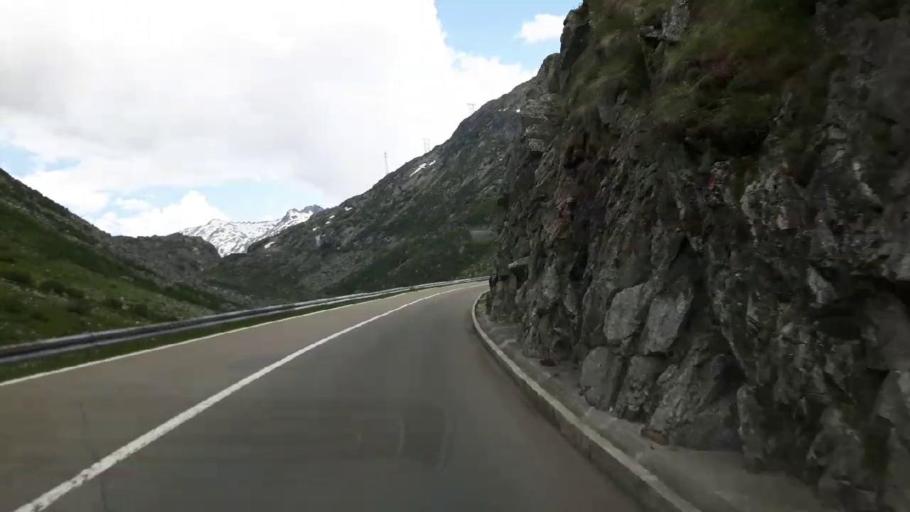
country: CH
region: Uri
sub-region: Uri
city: Andermatt
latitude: 46.5921
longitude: 8.5626
